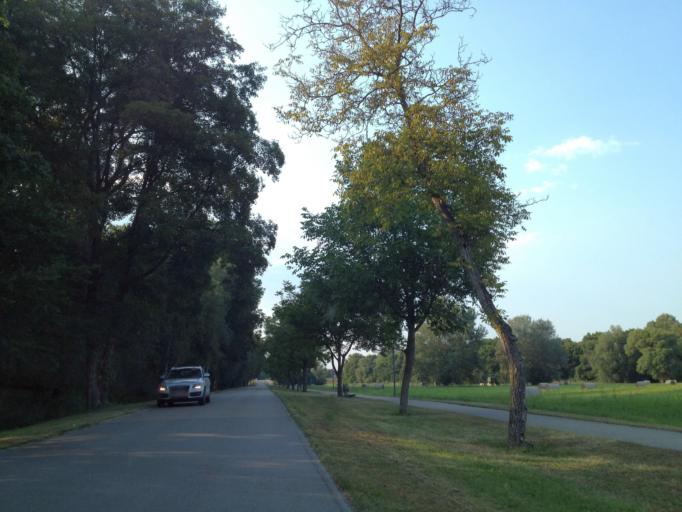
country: AT
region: Lower Austria
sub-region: Politischer Bezirk Ganserndorf
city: Orth an der Donau
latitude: 48.1299
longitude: 16.7081
